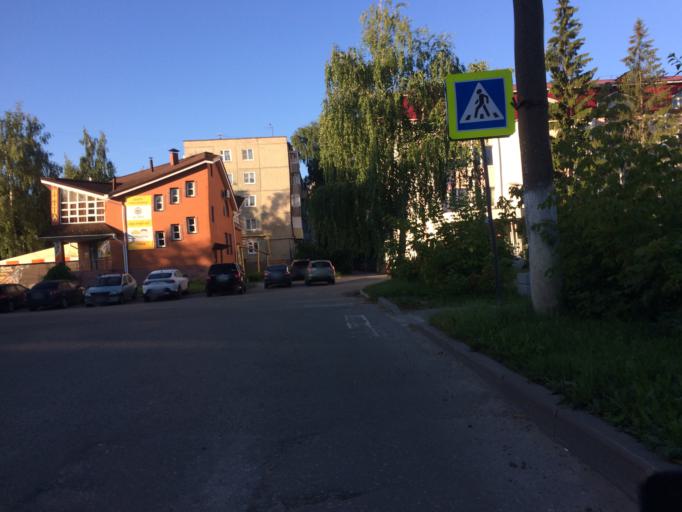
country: RU
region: Mariy-El
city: Yoshkar-Ola
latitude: 56.6419
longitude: 47.8783
